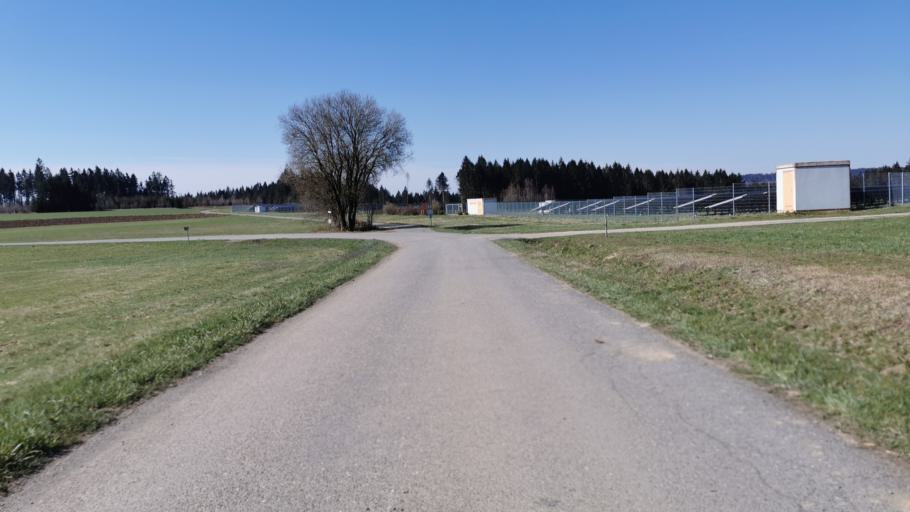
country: DE
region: Bavaria
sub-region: Upper Franconia
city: Teuschnitz
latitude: 50.4038
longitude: 11.3330
